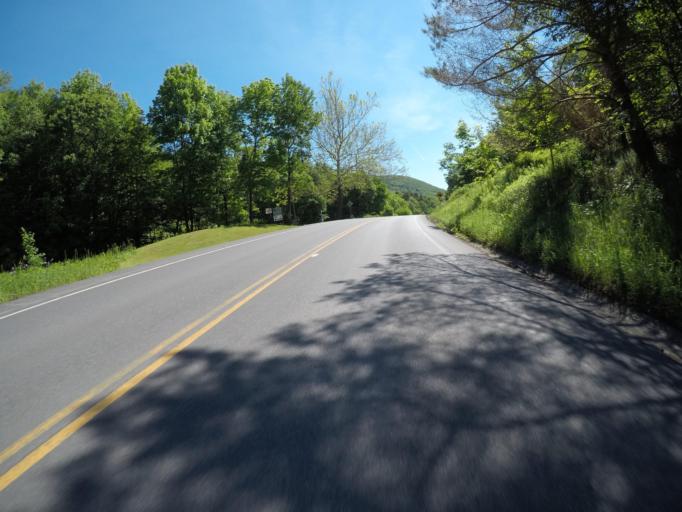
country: US
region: New York
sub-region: Delaware County
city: Delhi
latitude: 42.2582
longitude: -74.9546
